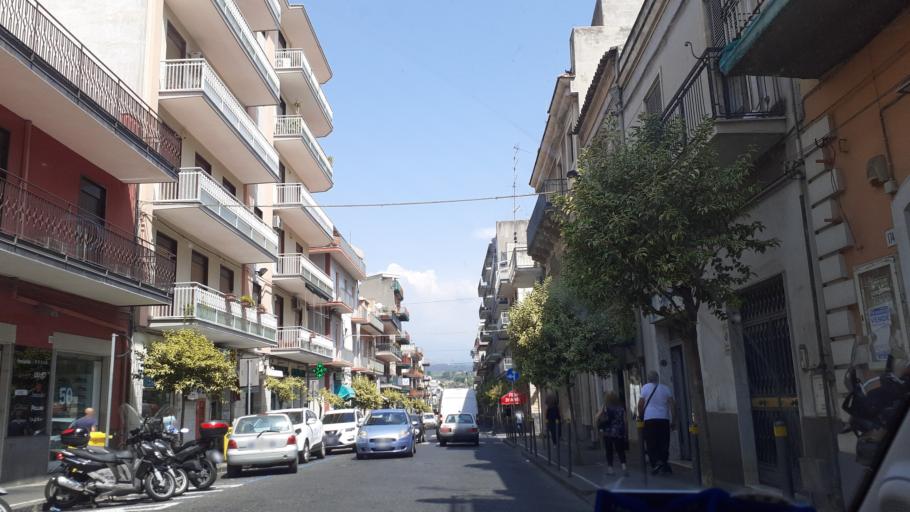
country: IT
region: Sicily
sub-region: Catania
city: Belvedere-Piano Tavola
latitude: 37.5187
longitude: 15.0071
